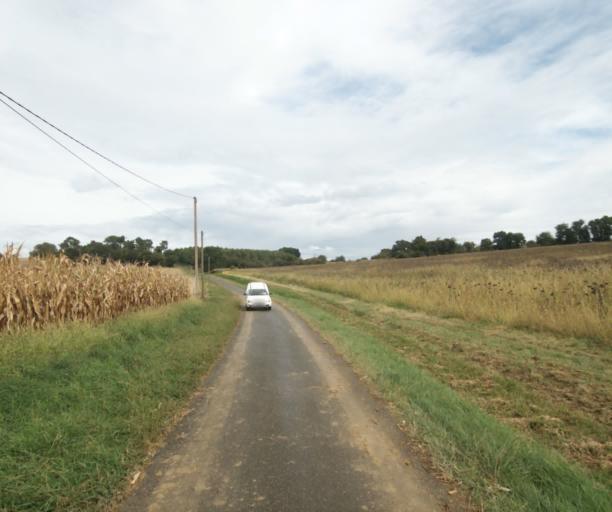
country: FR
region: Midi-Pyrenees
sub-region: Departement du Gers
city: Cazaubon
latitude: 43.8998
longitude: -0.1342
